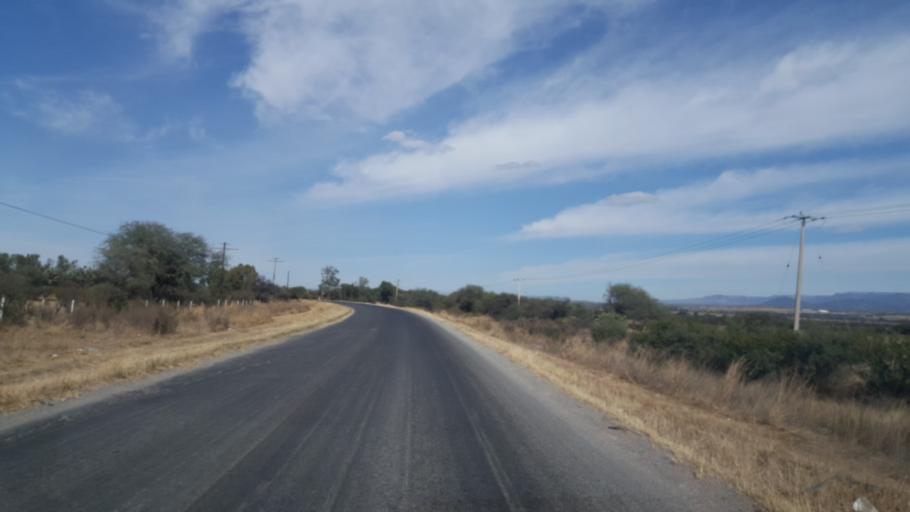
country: MX
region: Jalisco
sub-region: Lagos de Moreno
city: Geovillas Laureles del Campanario
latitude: 21.2941
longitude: -101.9297
